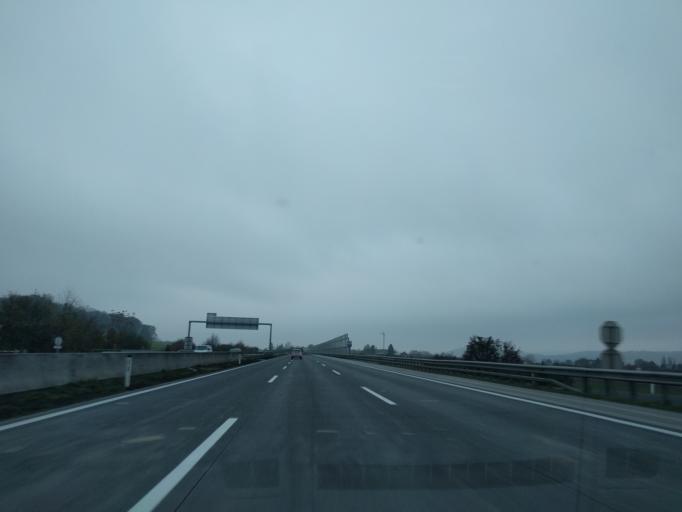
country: AT
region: Lower Austria
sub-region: Politischer Bezirk Melk
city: Melk
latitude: 48.2175
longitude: 15.3335
